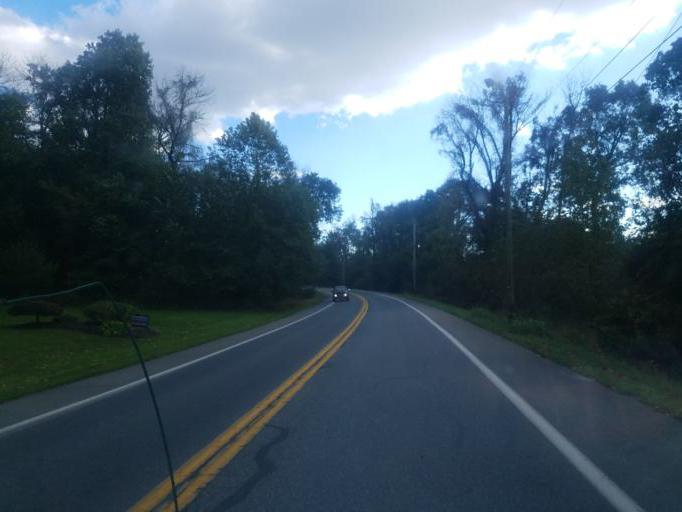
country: US
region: Pennsylvania
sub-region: Lancaster County
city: Bainbridge
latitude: 40.1257
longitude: -76.7141
